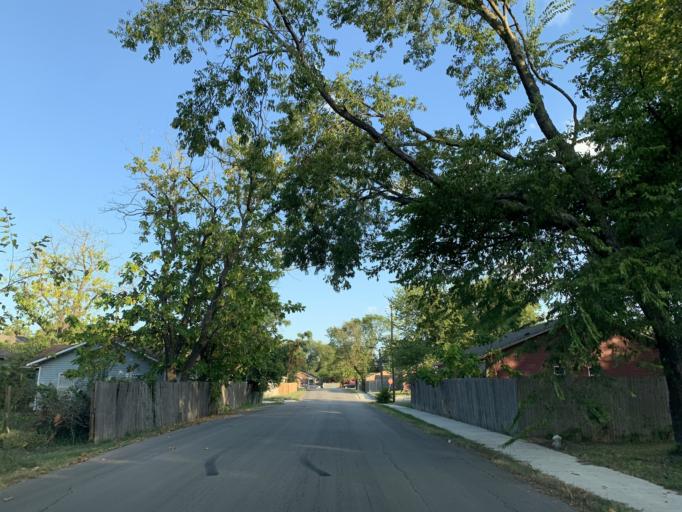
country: US
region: Texas
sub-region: Dallas County
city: Dallas
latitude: 32.7039
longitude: -96.7848
